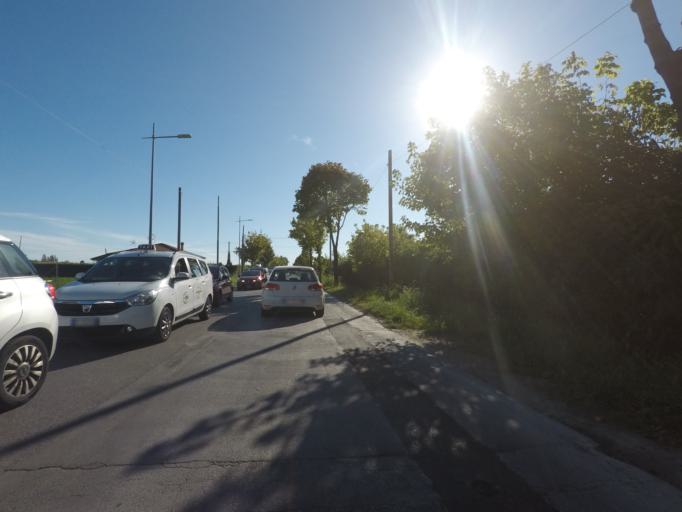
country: IT
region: Tuscany
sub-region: Provincia di Lucca
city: Piano di Mommio
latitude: 43.9271
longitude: 10.2696
